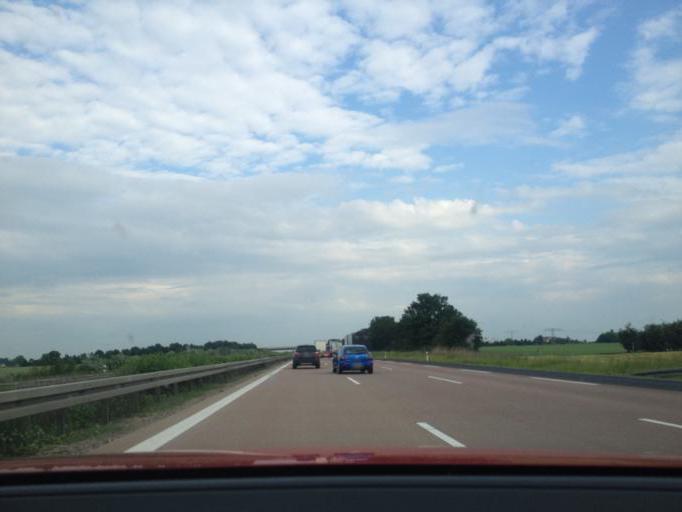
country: DE
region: Saxony-Anhalt
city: Grobers
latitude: 51.4547
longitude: 12.1119
